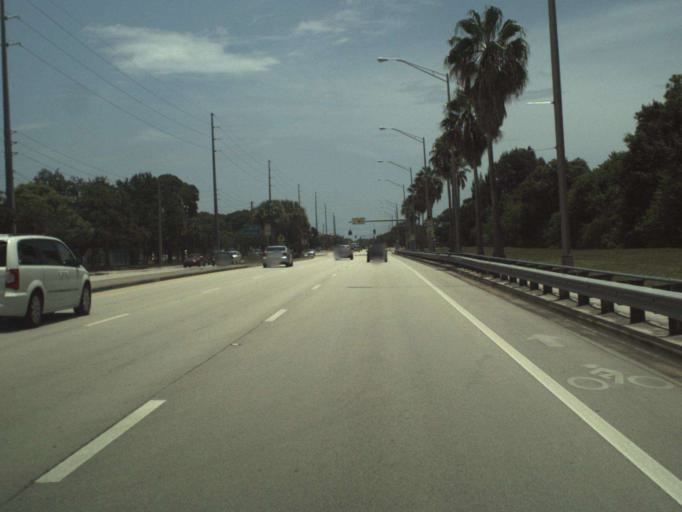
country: US
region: Florida
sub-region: Saint Lucie County
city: Fort Pierce South
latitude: 27.4254
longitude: -80.3398
